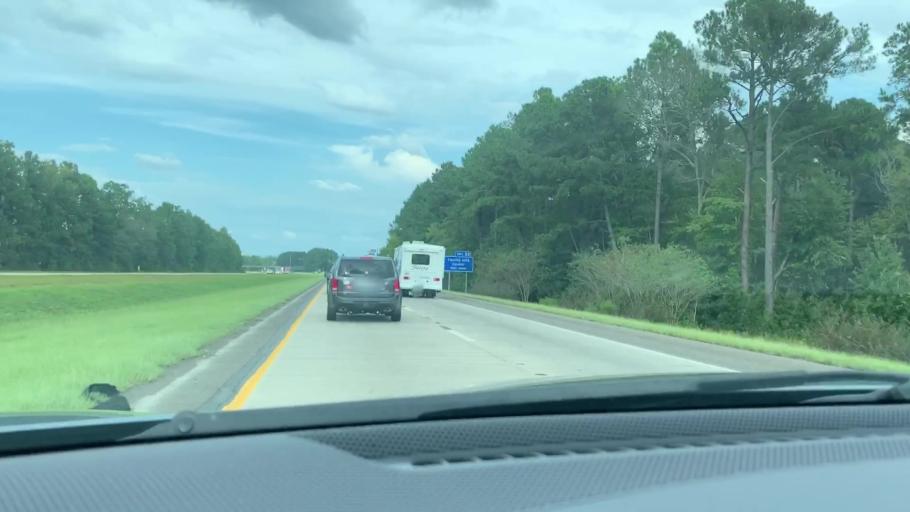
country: US
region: South Carolina
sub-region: Colleton County
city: Walterboro
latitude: 32.8714
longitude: -80.7204
